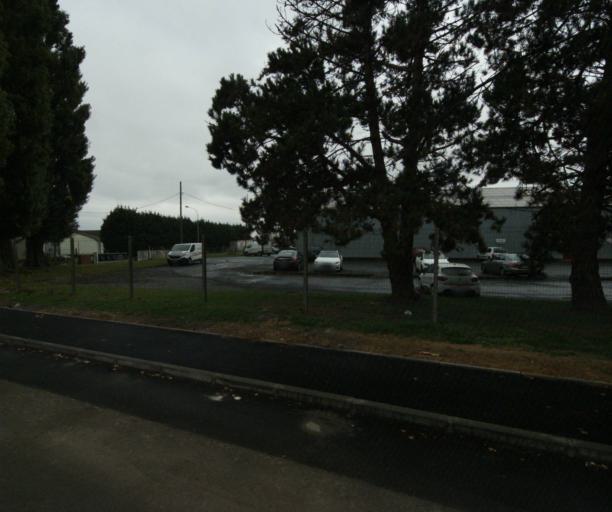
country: FR
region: Nord-Pas-de-Calais
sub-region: Departement du Nord
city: Santes
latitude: 50.6057
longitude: 2.9522
